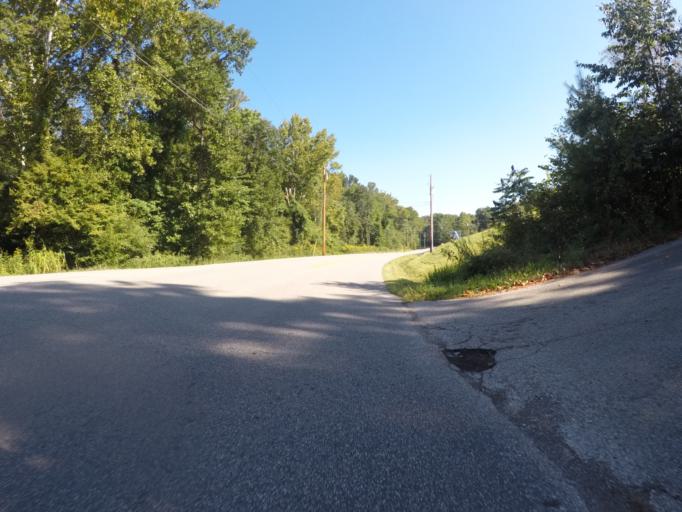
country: US
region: Kentucky
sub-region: Greenup County
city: Russell
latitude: 38.5090
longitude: -82.6956
